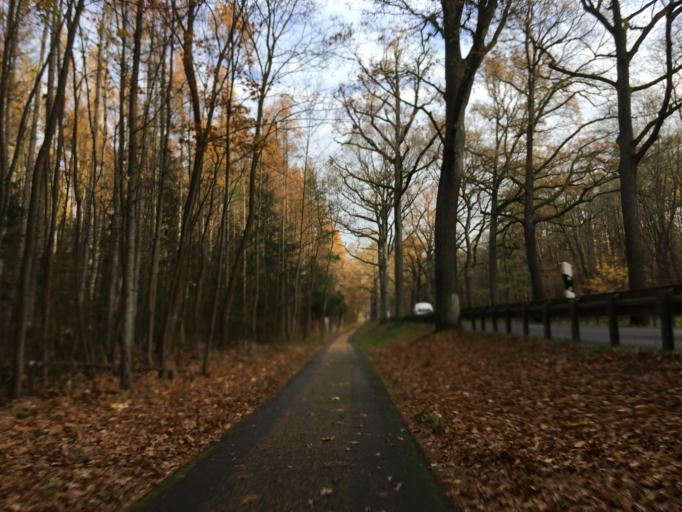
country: DE
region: Brandenburg
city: Tauer
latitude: 51.9250
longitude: 14.5072
